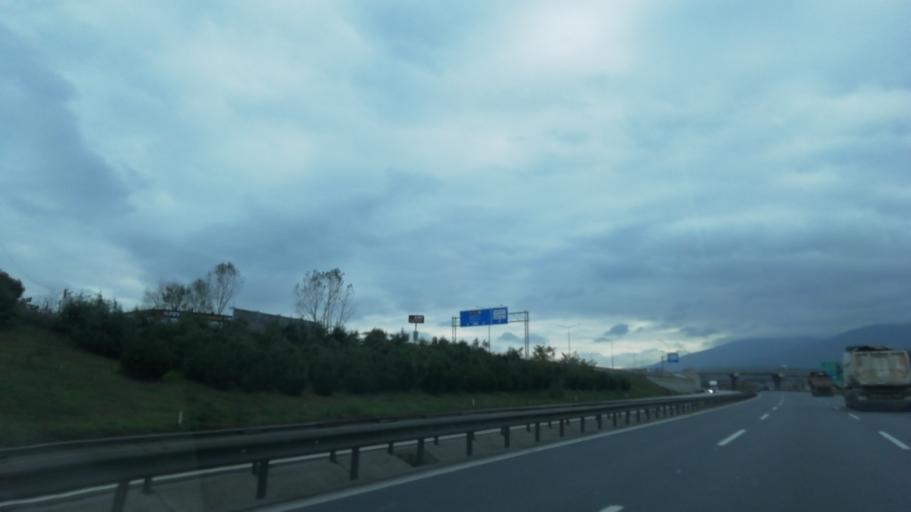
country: TR
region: Kocaeli
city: Kosekoy
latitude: 40.7340
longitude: 30.0530
